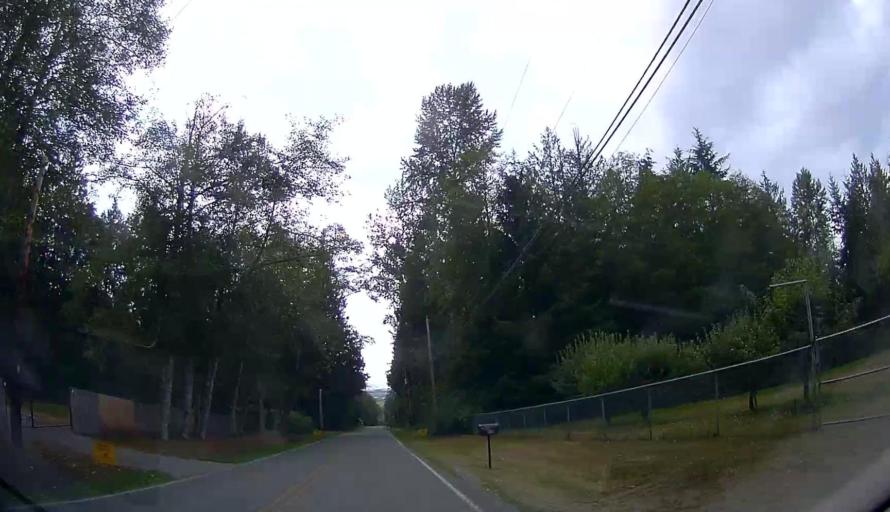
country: US
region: Washington
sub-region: Skagit County
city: Burlington
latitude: 48.5824
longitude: -122.3955
